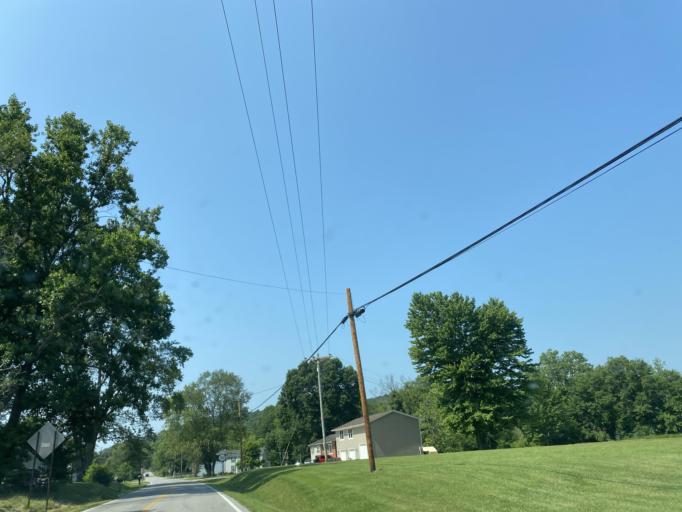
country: US
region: Kentucky
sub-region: Campbell County
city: Claryville
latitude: 38.8696
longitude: -84.4556
